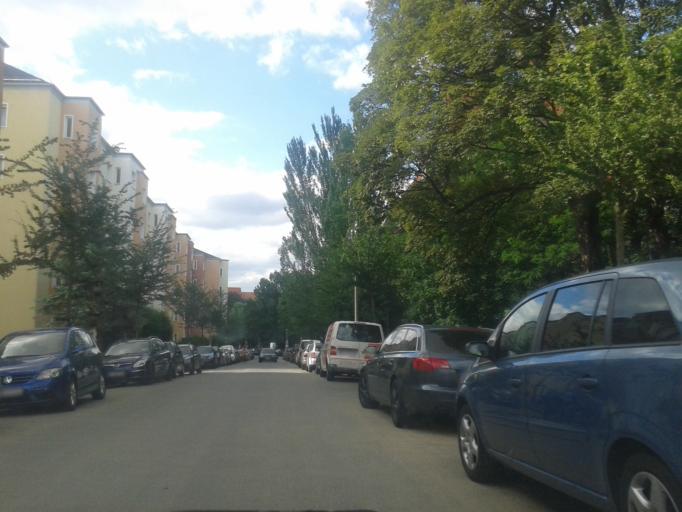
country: DE
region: Saxony
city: Dresden
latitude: 51.0281
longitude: 13.7218
